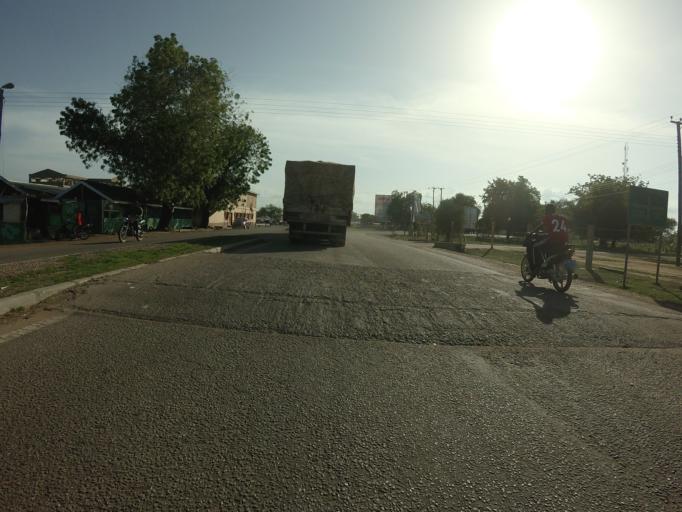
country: GH
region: Upper East
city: Navrongo
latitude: 10.8963
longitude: -1.0906
